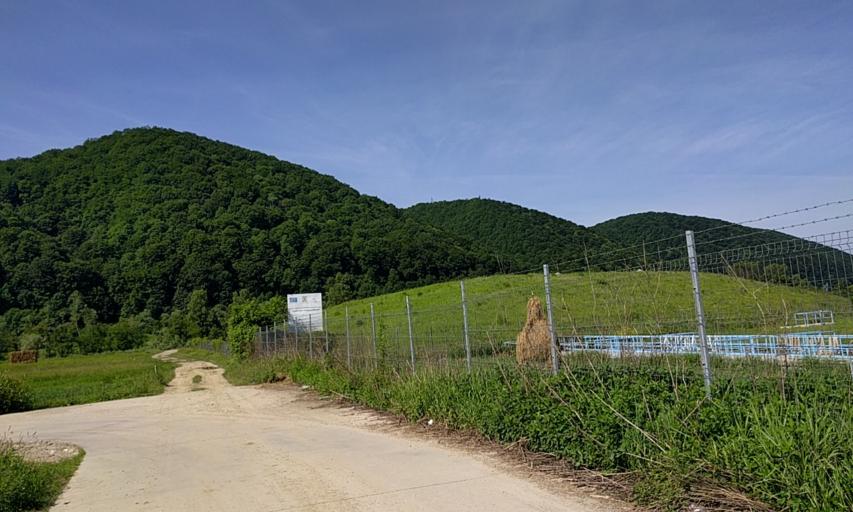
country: RO
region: Bistrita-Nasaud
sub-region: Oras Nasaud
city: Nasaud
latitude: 47.2938
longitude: 24.3786
